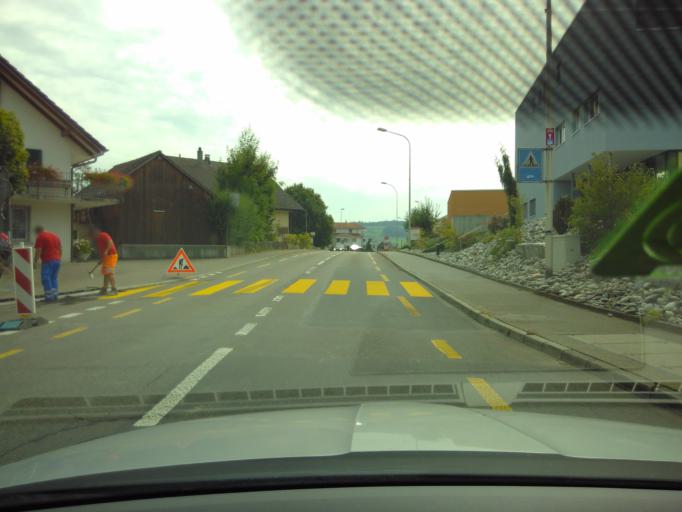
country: CH
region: Lucerne
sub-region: Sursee District
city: Gunzwil
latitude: 47.2115
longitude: 8.1781
